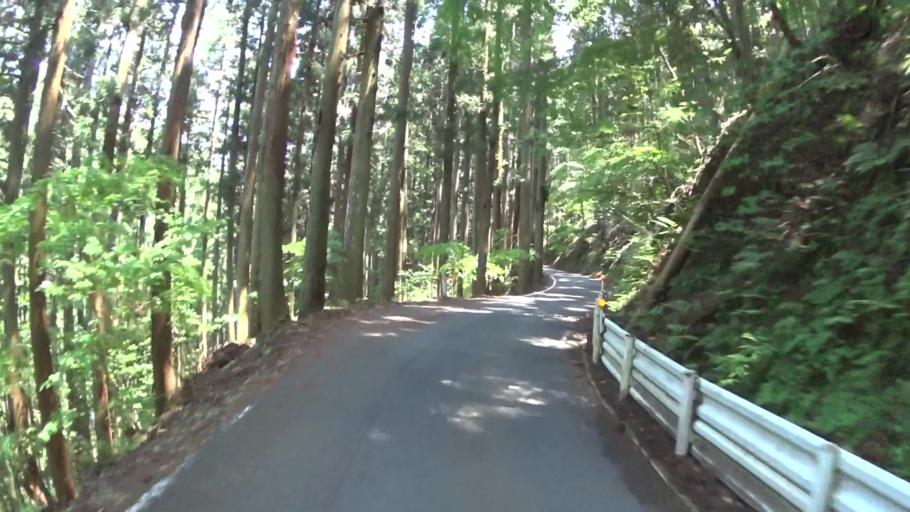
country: JP
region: Kyoto
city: Kameoka
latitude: 35.1227
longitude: 135.5846
